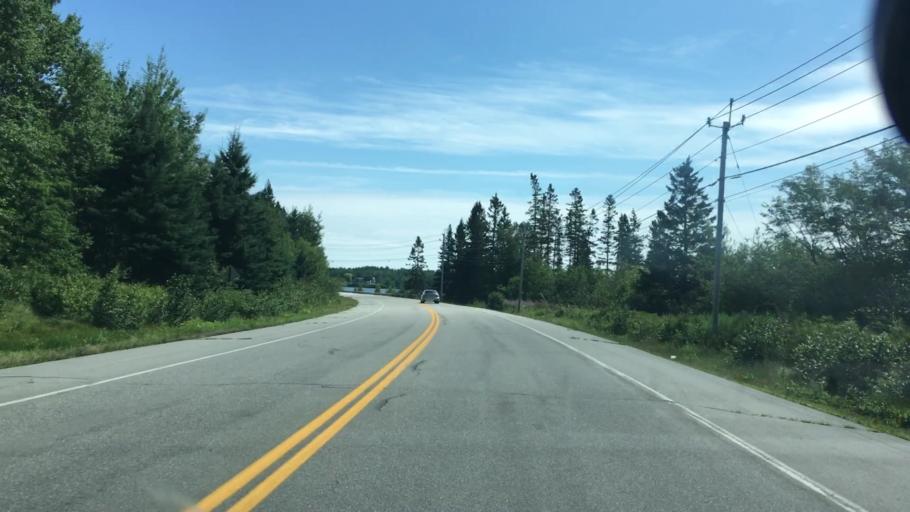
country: US
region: Maine
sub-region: Washington County
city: Eastport
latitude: 44.9421
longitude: -67.0383
